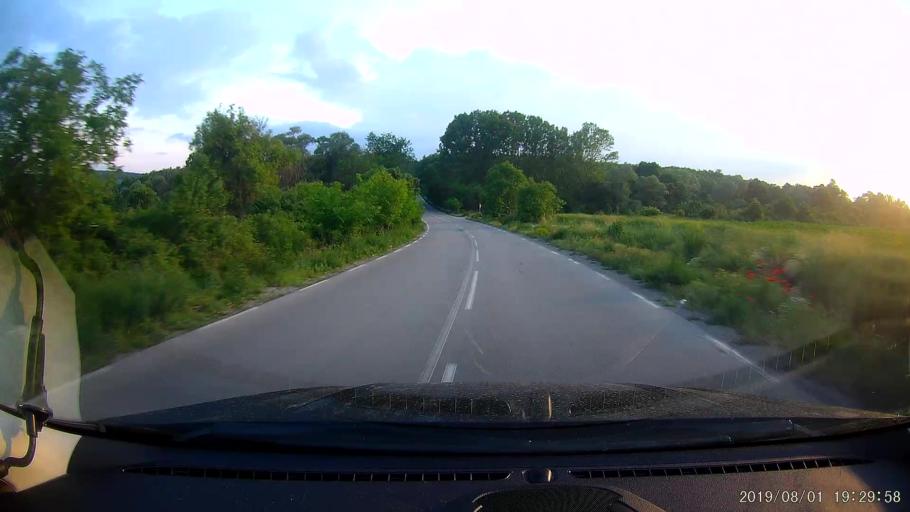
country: BG
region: Burgas
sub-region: Obshtina Sungurlare
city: Sungurlare
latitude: 42.8199
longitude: 26.8979
